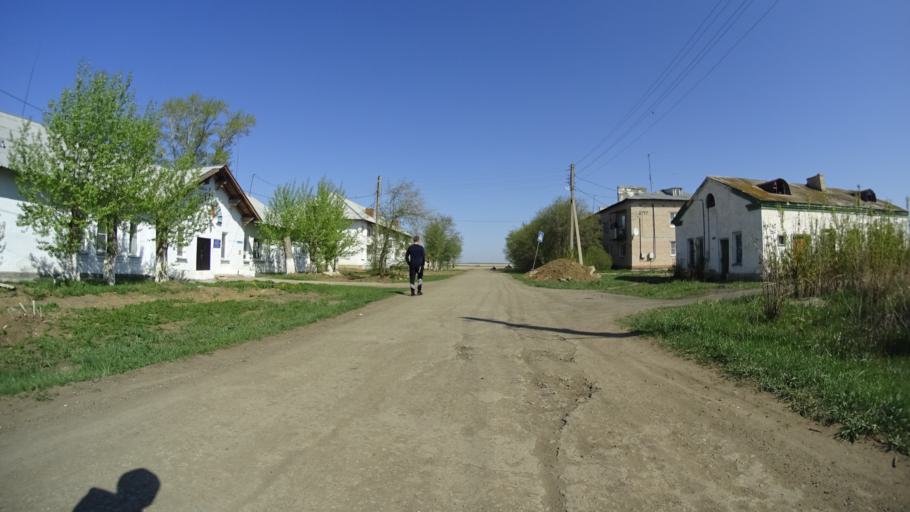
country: RU
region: Chelyabinsk
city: Troitsk
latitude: 54.1897
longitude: 61.5063
